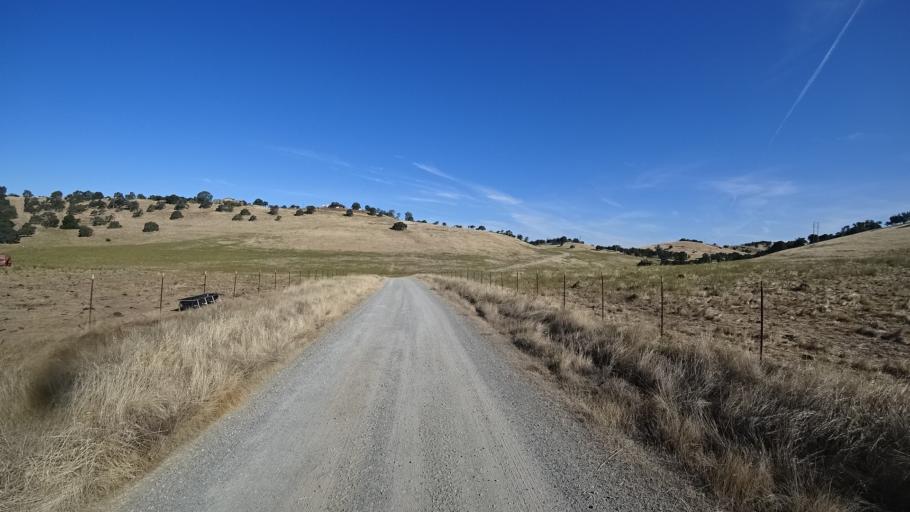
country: US
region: California
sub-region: Calaveras County
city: Valley Springs
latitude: 38.2259
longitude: -120.7931
